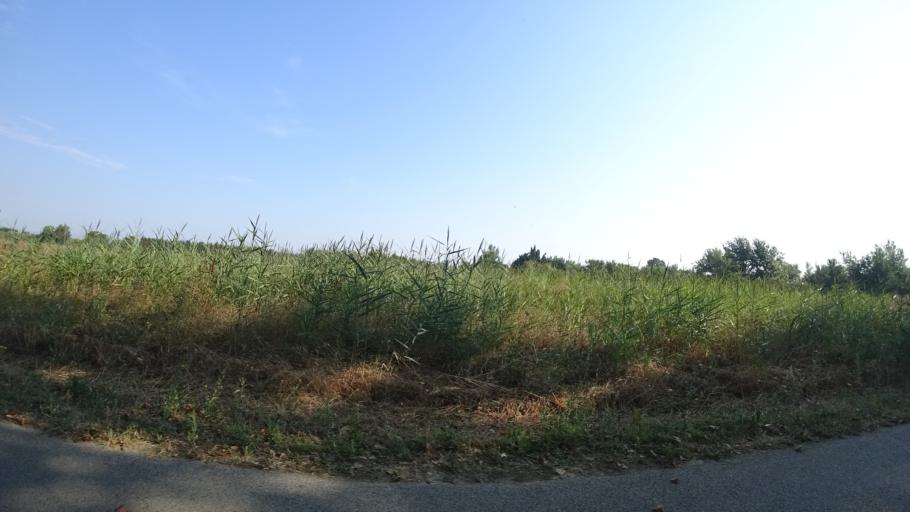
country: FR
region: Languedoc-Roussillon
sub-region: Departement des Pyrenees-Orientales
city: Villelongue-de-la-Salanque
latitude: 42.7259
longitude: 2.9610
